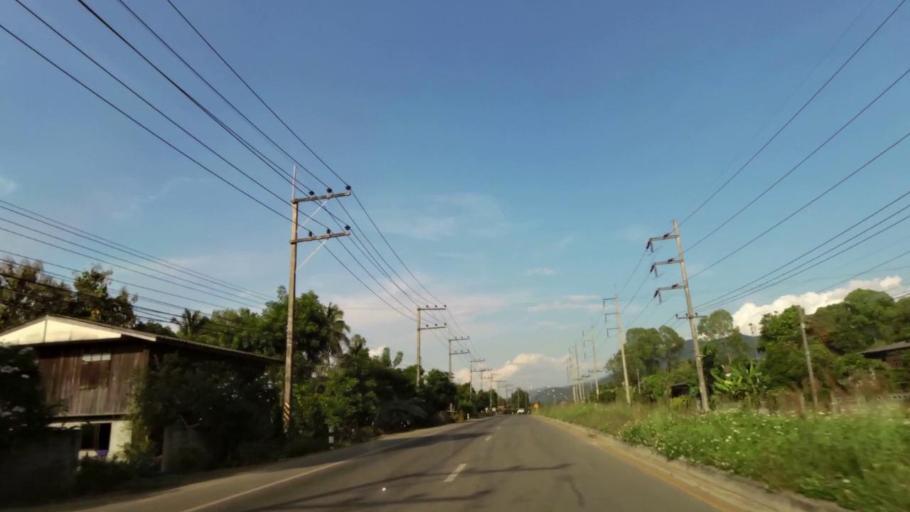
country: TH
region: Chiang Rai
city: Khun Tan
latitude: 19.8765
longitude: 100.2885
